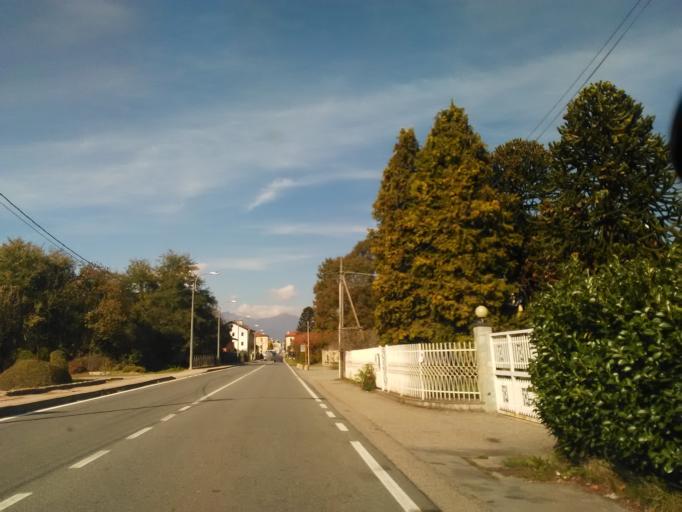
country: IT
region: Piedmont
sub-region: Provincia di Vercelli
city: Serravalle Sesia
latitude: 45.6731
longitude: 8.3234
